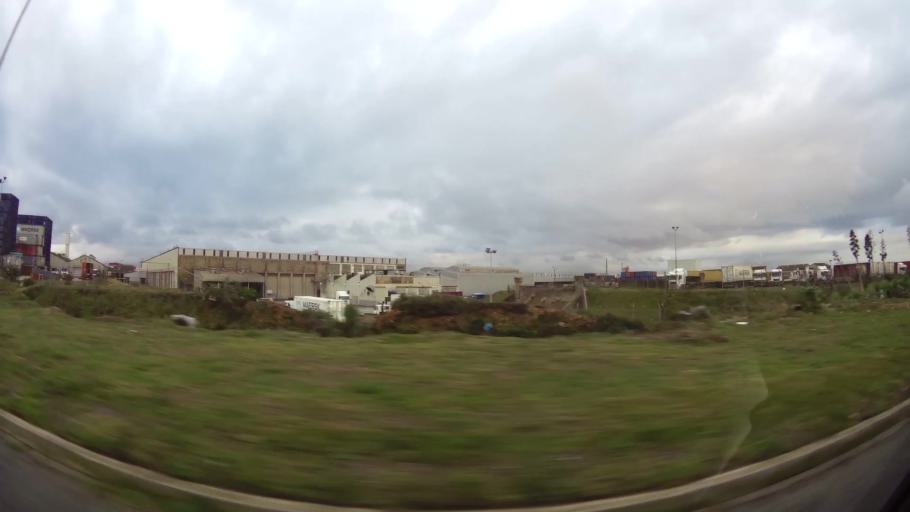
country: ZA
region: Eastern Cape
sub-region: Nelson Mandela Bay Metropolitan Municipality
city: Port Elizabeth
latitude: -33.9230
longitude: 25.6007
